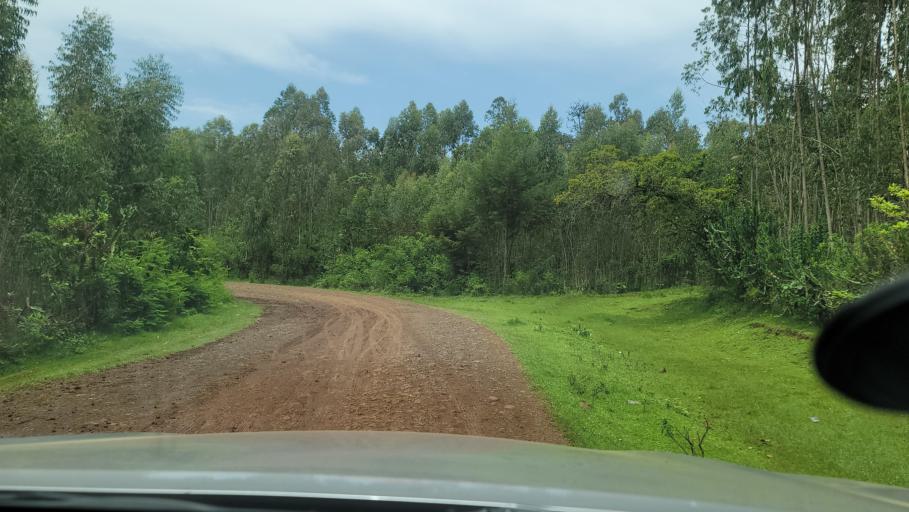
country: ET
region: Oromiya
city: Agaro
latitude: 7.7338
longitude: 36.2596
